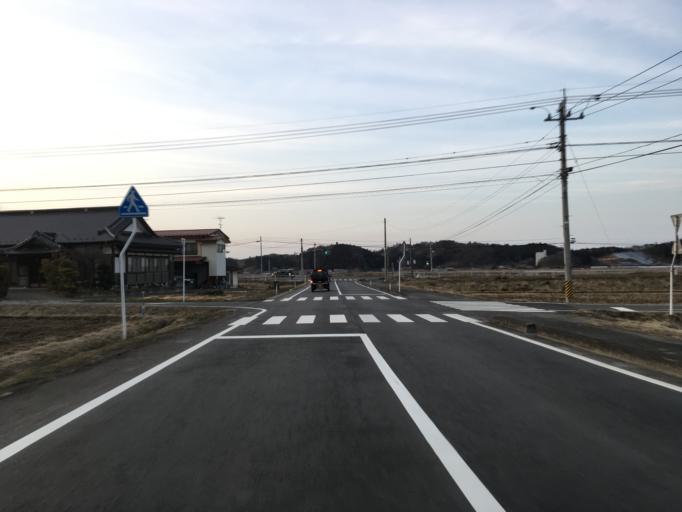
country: JP
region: Fukushima
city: Ishikawa
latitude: 37.0557
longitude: 140.3320
